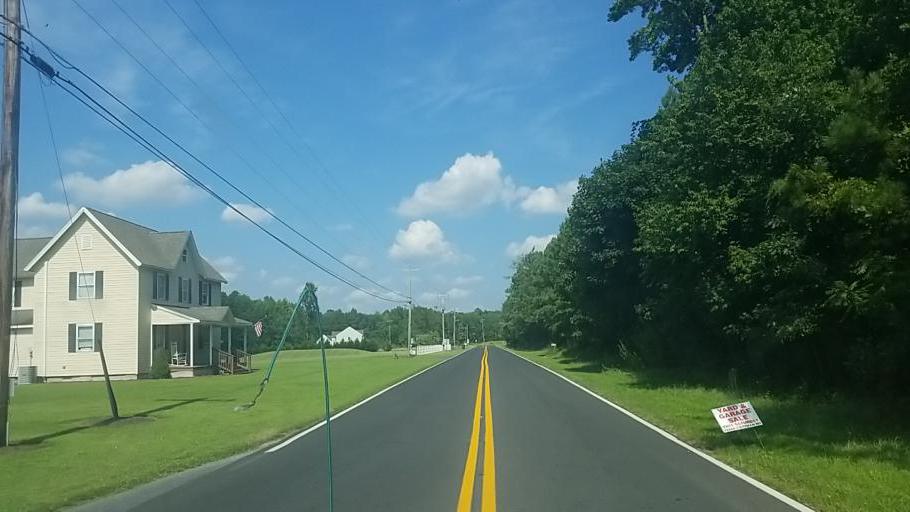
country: US
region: Maryland
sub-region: Wicomico County
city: Fruitland
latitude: 38.3118
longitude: -75.6482
